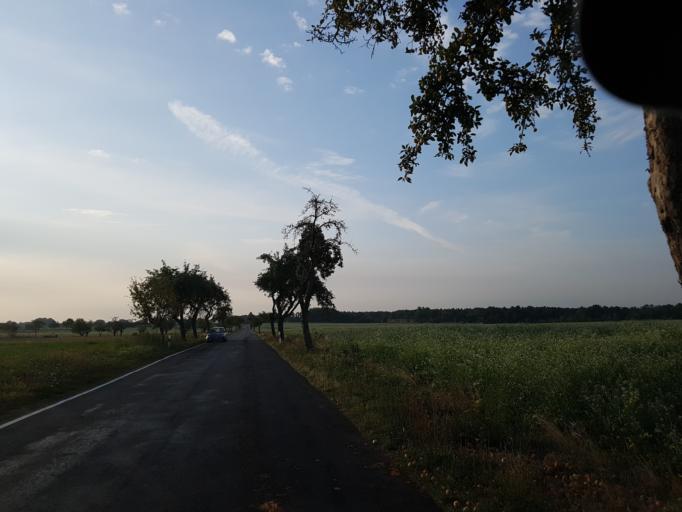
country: DE
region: Brandenburg
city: Hohenleipisch
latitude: 51.4898
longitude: 13.5698
